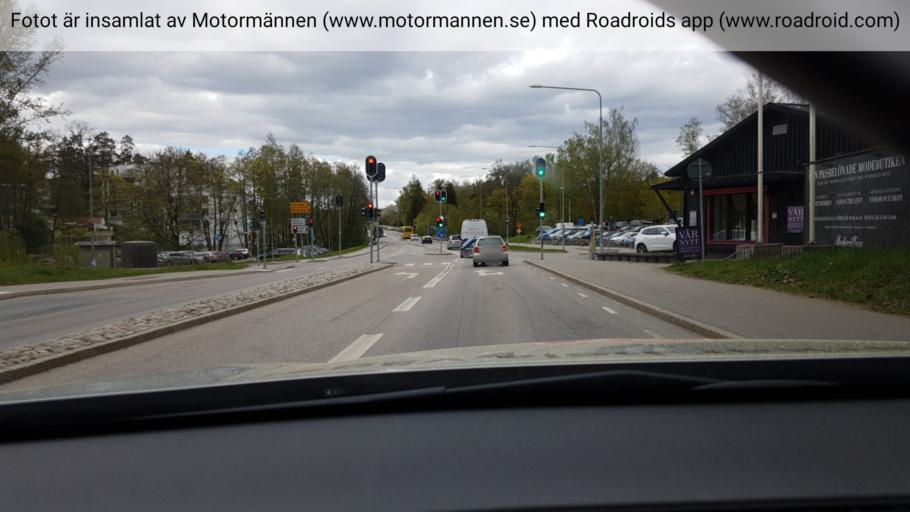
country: SE
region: Stockholm
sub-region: Tyreso Kommun
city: Bollmora
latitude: 59.2097
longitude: 18.2081
